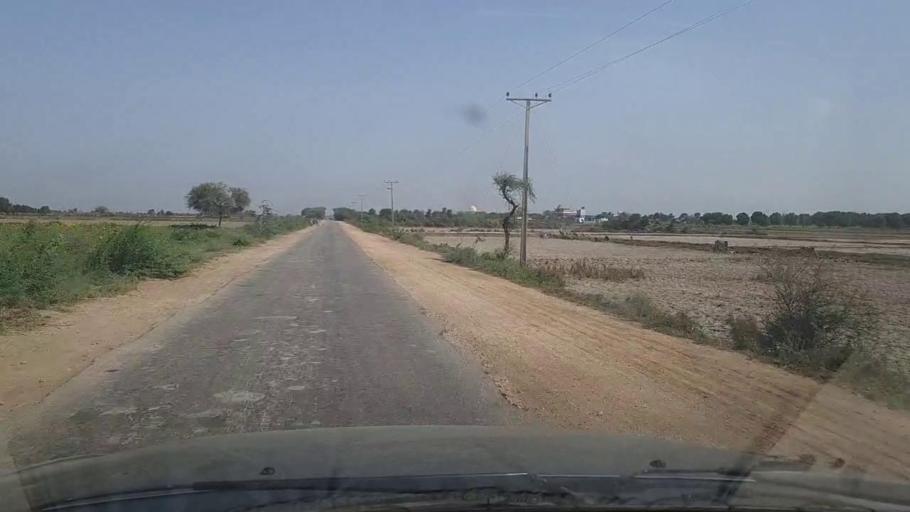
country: PK
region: Sindh
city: Mirpur Batoro
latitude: 24.6349
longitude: 68.2922
